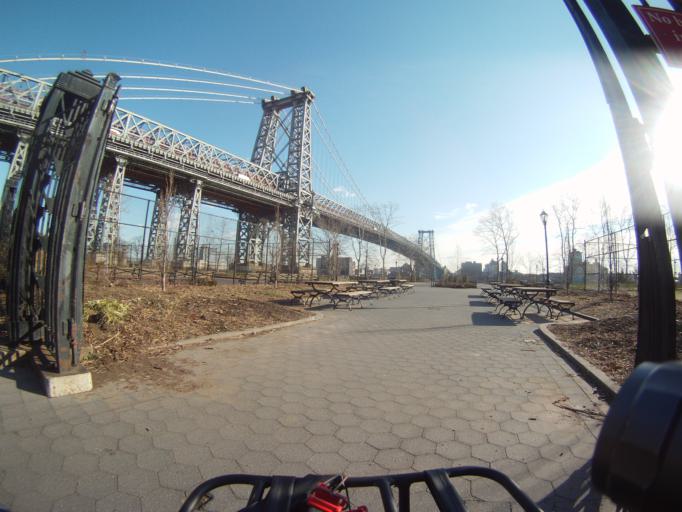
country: US
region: New York
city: New York City
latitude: 40.7142
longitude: -73.9766
